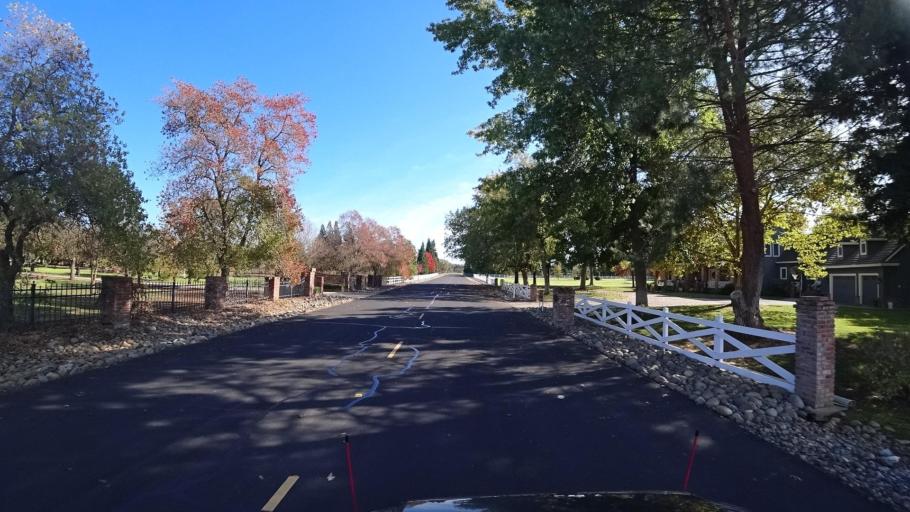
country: US
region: California
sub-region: Sacramento County
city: Wilton
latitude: 38.4327
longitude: -121.2784
